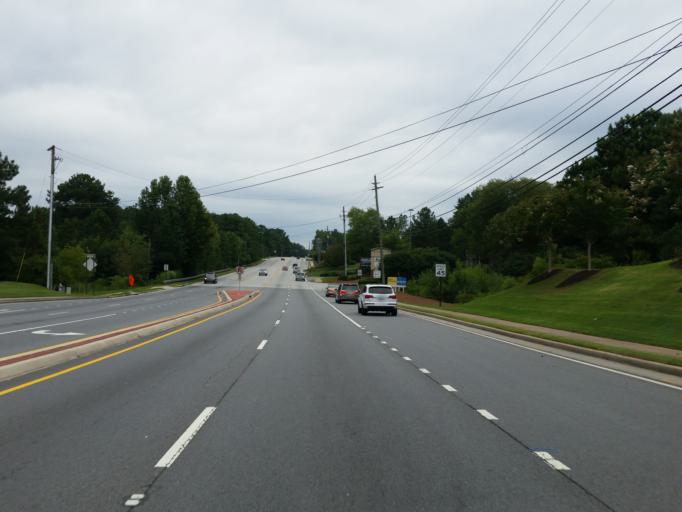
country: US
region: Georgia
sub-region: Cobb County
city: Fair Oaks
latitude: 33.9044
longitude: -84.6044
